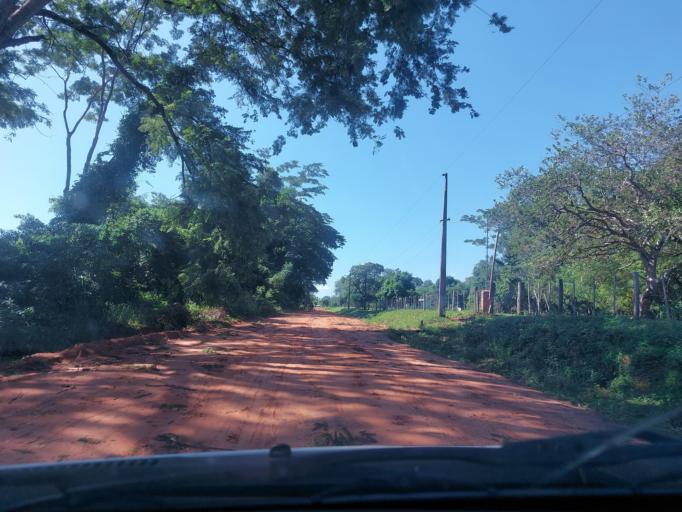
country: PY
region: San Pedro
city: Itacurubi del Rosario
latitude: -24.5389
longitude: -56.5809
